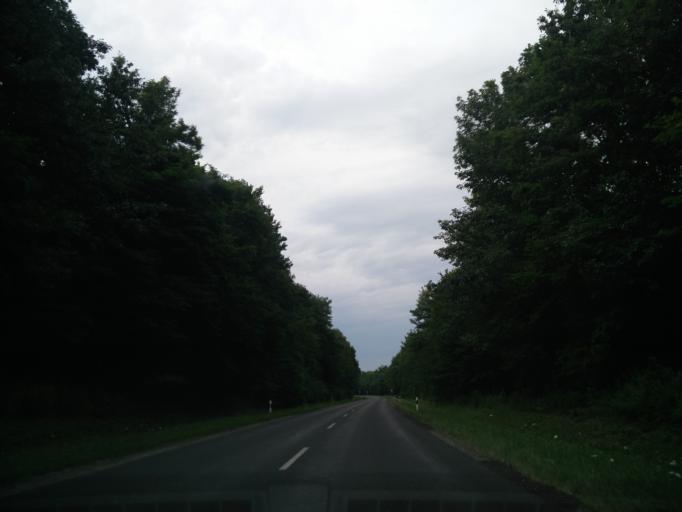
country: HU
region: Vas
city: Vasvar
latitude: 47.0022
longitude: 16.8281
